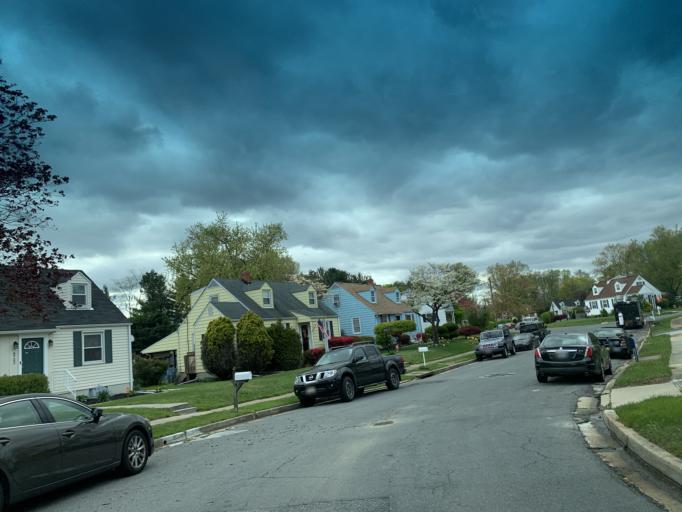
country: US
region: Maryland
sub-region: Baltimore County
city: Parkville
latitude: 39.3995
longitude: -76.5618
